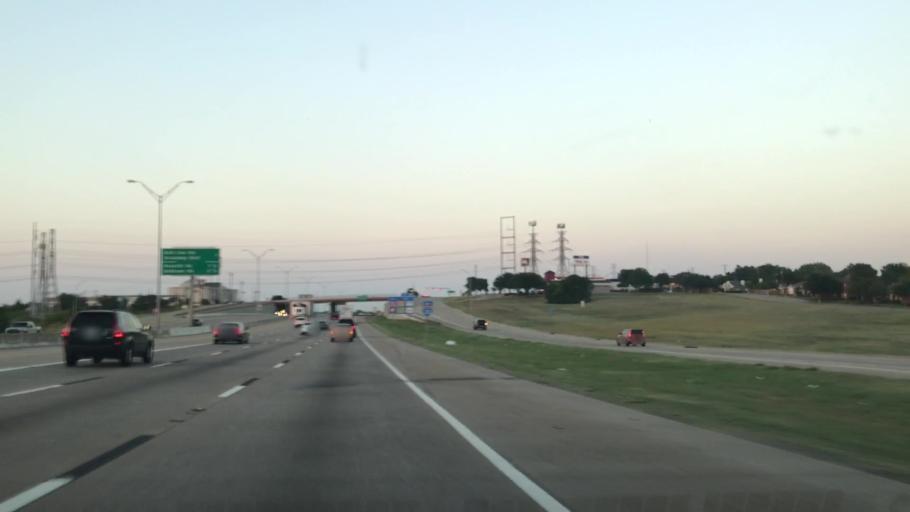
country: US
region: Texas
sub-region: Dallas County
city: Sunnyvale
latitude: 32.8305
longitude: -96.6169
